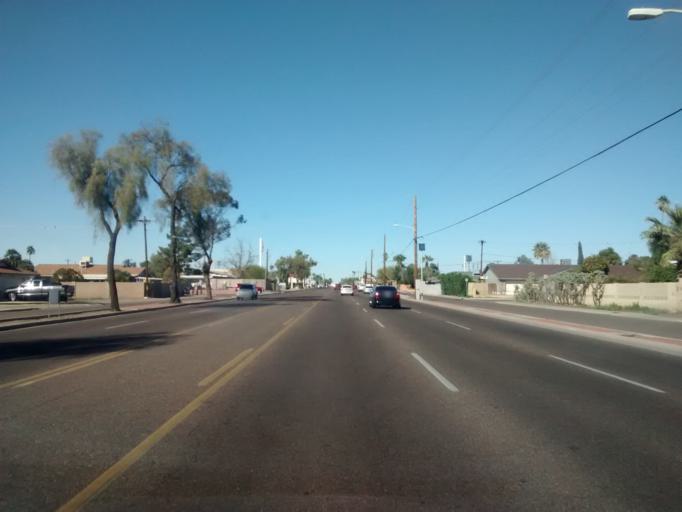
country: US
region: Arizona
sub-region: Maricopa County
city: Glendale
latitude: 33.5484
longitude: -112.1343
